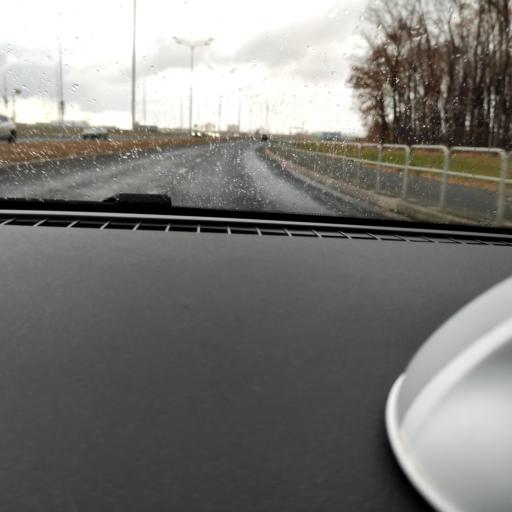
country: RU
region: Samara
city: Petra-Dubrava
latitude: 53.2798
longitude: 50.2479
